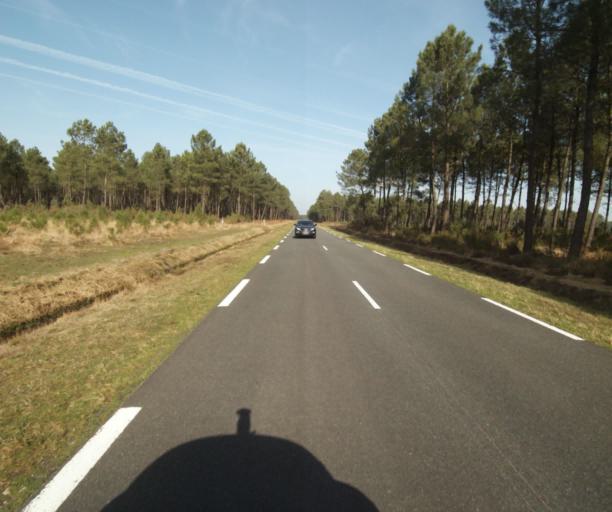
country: FR
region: Aquitaine
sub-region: Departement du Lot-et-Garonne
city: Casteljaloux
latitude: 44.1643
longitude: 0.0583
